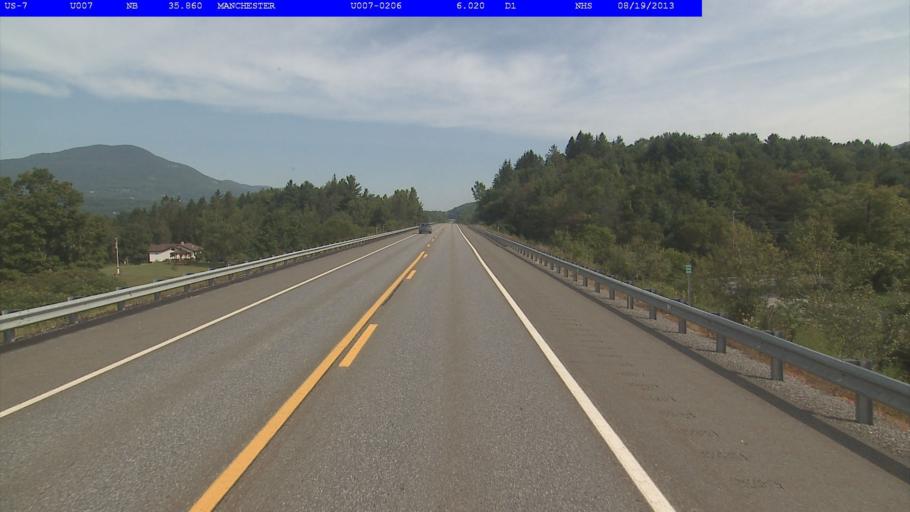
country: US
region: Vermont
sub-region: Bennington County
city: Manchester Center
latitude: 43.1891
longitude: -73.0147
